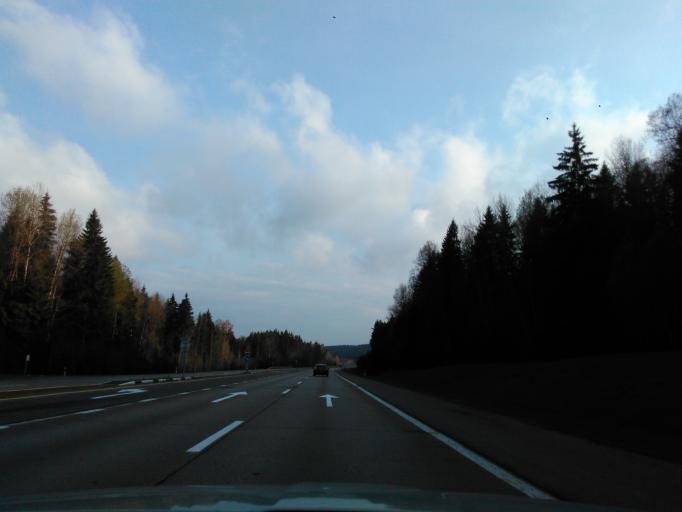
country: BY
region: Minsk
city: Lahoysk
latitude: 54.1221
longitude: 27.8071
